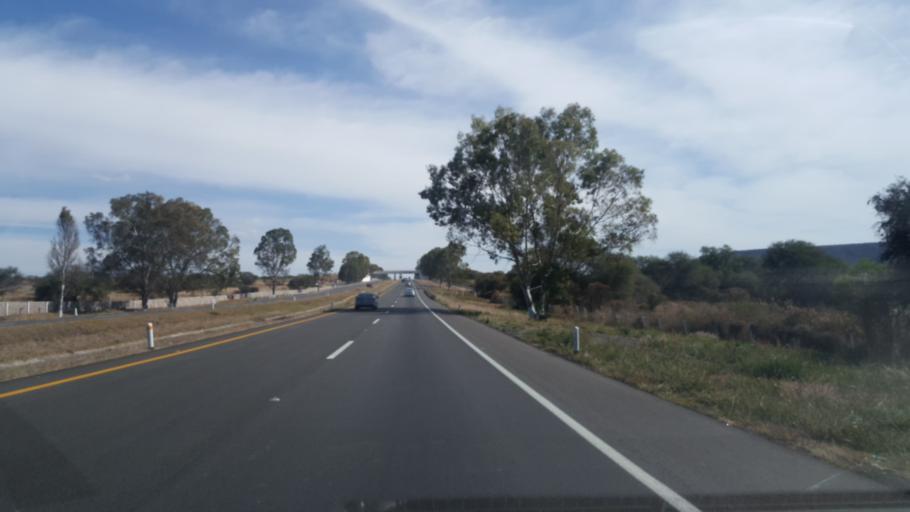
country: MX
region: Jalisco
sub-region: Lagos de Moreno
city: Cristeros [Fraccionamiento]
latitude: 21.2796
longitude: -101.9911
